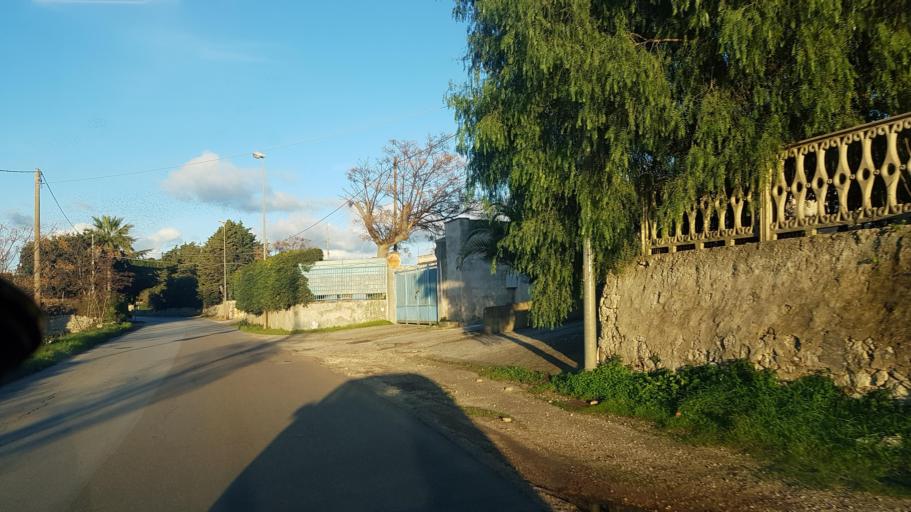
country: IT
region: Apulia
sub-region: Provincia di Brindisi
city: Ostuni
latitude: 40.7220
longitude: 17.5675
